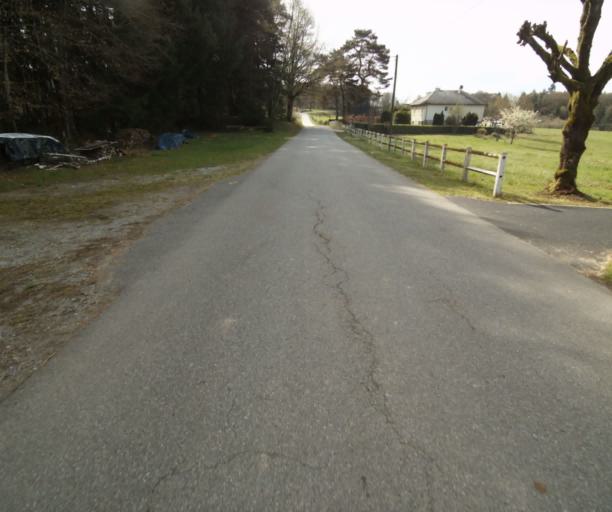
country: FR
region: Limousin
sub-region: Departement de la Correze
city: Correze
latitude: 45.3496
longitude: 1.8737
